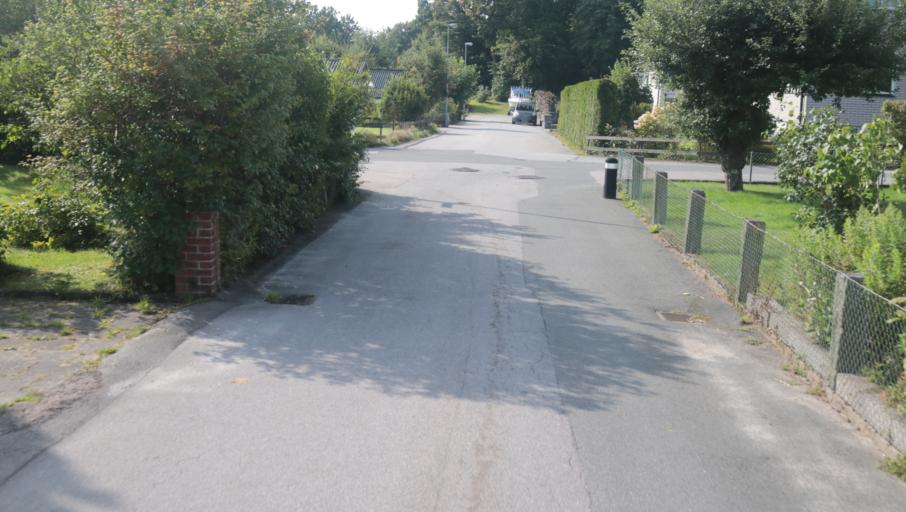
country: SE
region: Blekinge
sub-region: Karlshamns Kommun
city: Karlshamn
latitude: 56.1907
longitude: 14.8525
